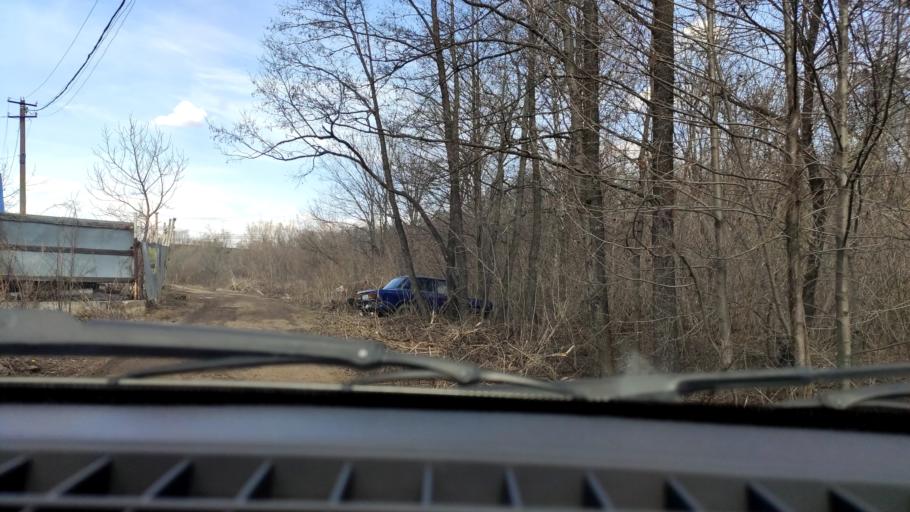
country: RU
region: Bashkortostan
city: Avdon
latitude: 54.6806
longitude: 55.8210
